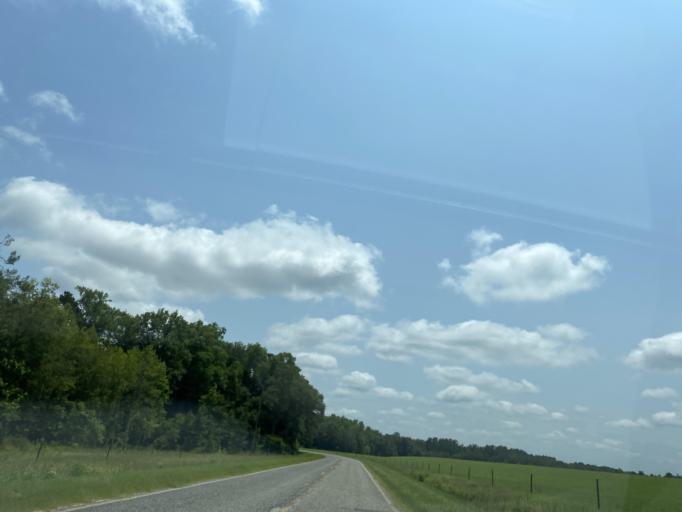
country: US
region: Georgia
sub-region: Telfair County
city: Lumber City
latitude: 32.0067
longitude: -82.7210
